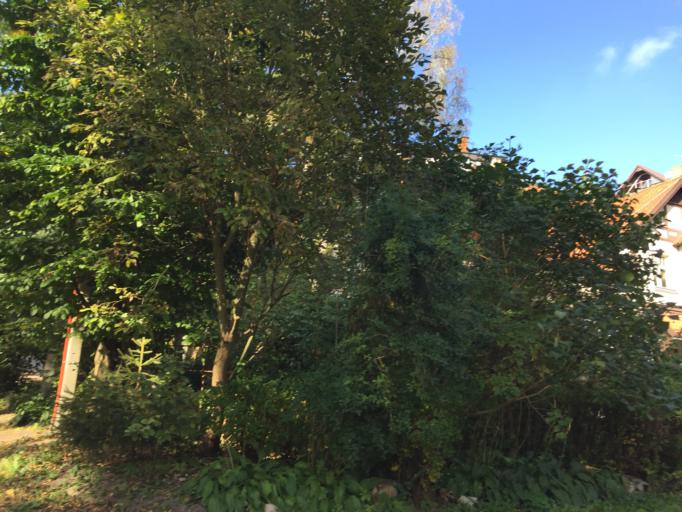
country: RU
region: Kaliningrad
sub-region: Gorod Svetlogorsk
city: Svetlogorsk
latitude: 54.9411
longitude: 20.1477
